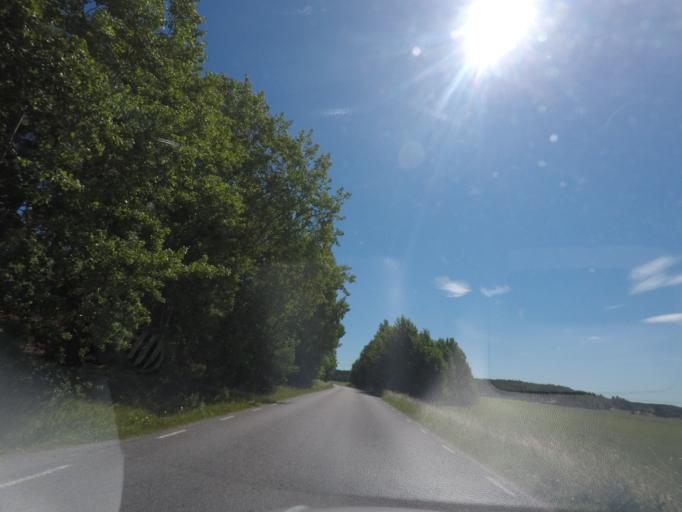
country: SE
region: Uppsala
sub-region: Enkopings Kommun
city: Irsta
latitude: 59.6751
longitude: 16.8680
